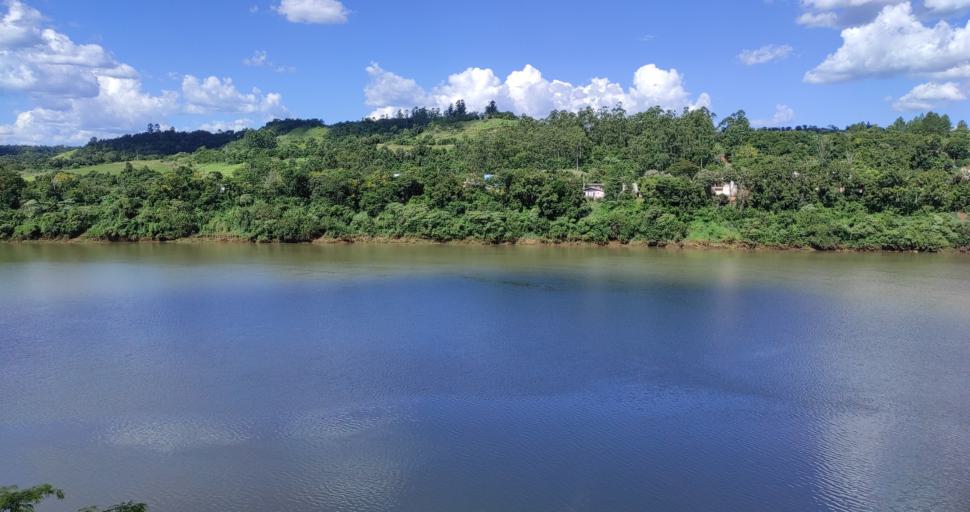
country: AR
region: Misiones
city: El Soberbio
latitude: -27.2973
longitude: -54.1939
